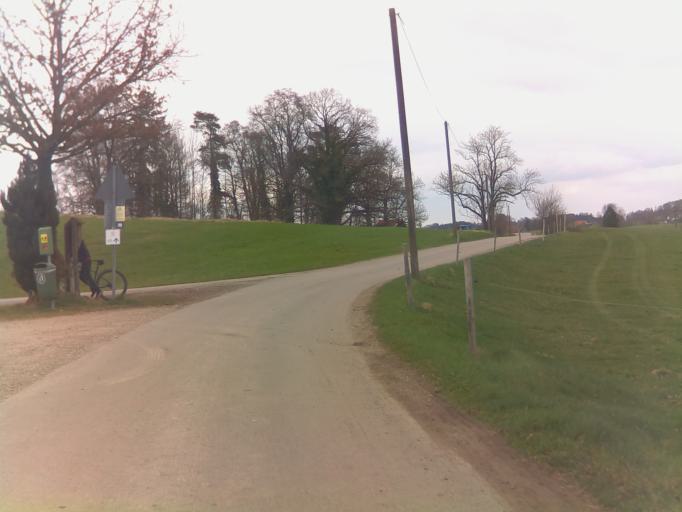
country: DE
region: Bavaria
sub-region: Upper Bavaria
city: Andechs
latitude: 47.9391
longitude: 11.2087
